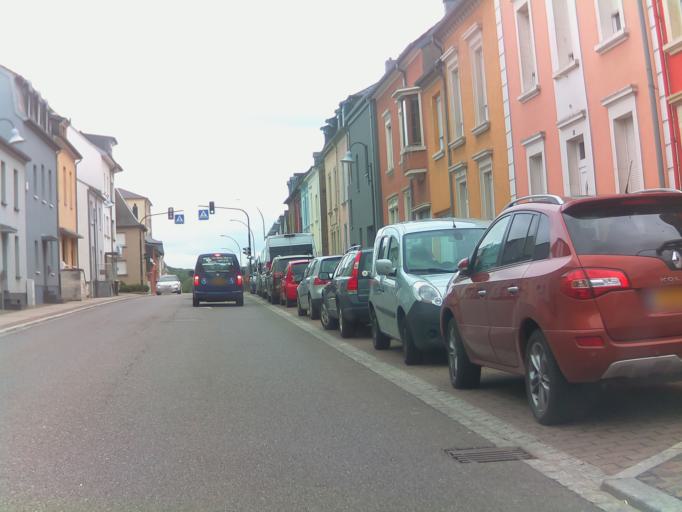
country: LU
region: Luxembourg
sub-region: Canton d'Esch-sur-Alzette
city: Bettembourg
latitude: 49.5152
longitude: 6.1056
